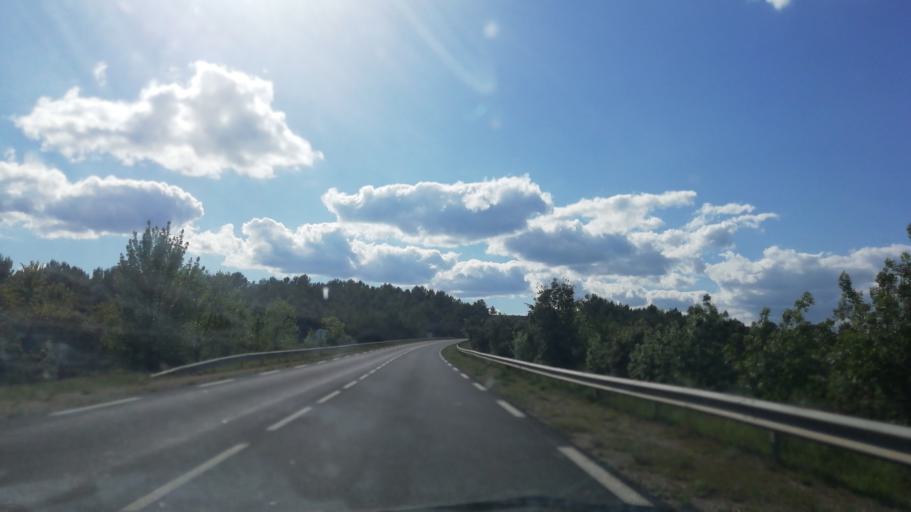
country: FR
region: Languedoc-Roussillon
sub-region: Departement de l'Herault
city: Saint-Gely-du-Fesc
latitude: 43.7088
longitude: 3.8050
